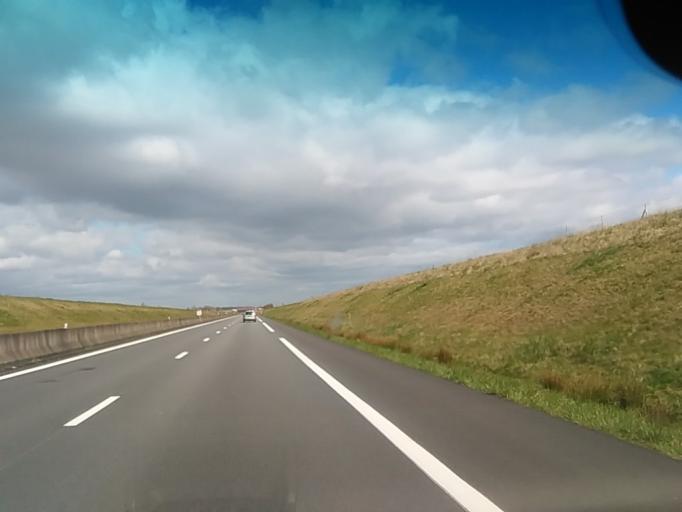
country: FR
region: Lower Normandy
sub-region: Departement du Calvados
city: Orbec
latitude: 49.0630
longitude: 0.4675
